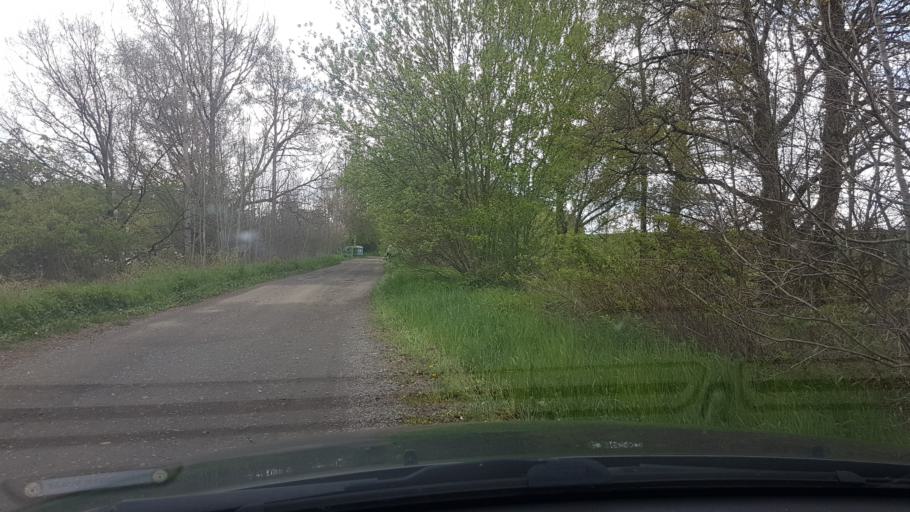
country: CZ
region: Karlovarsky
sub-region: Okres Cheb
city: Cheb
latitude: 50.0564
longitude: 12.3863
